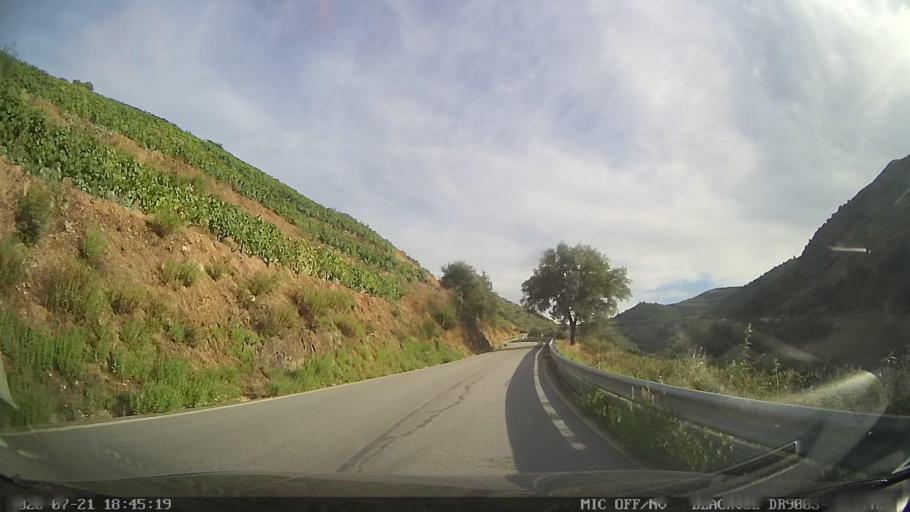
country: PT
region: Viseu
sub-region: Sao Joao da Pesqueira
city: Sao Joao da Pesqueira
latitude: 41.1221
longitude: -7.4491
